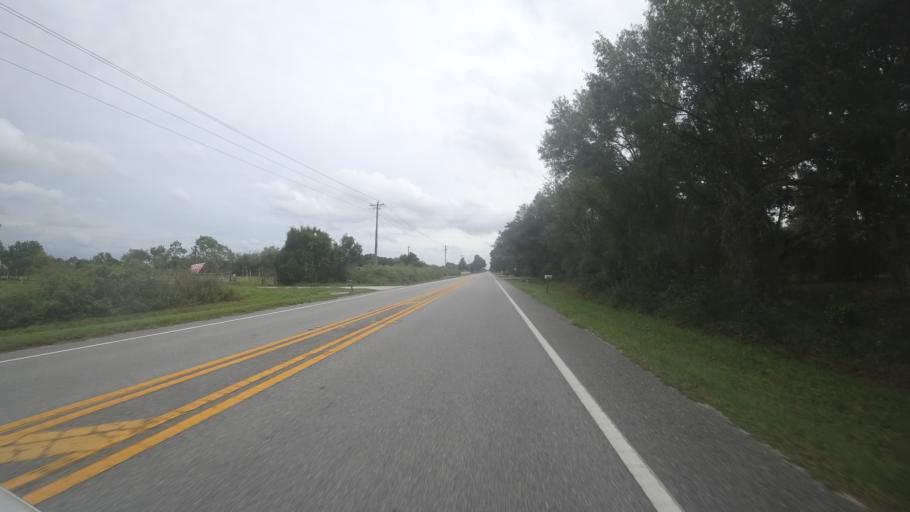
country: US
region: Florida
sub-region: Hillsborough County
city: Wimauma
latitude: 27.4599
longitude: -82.1185
